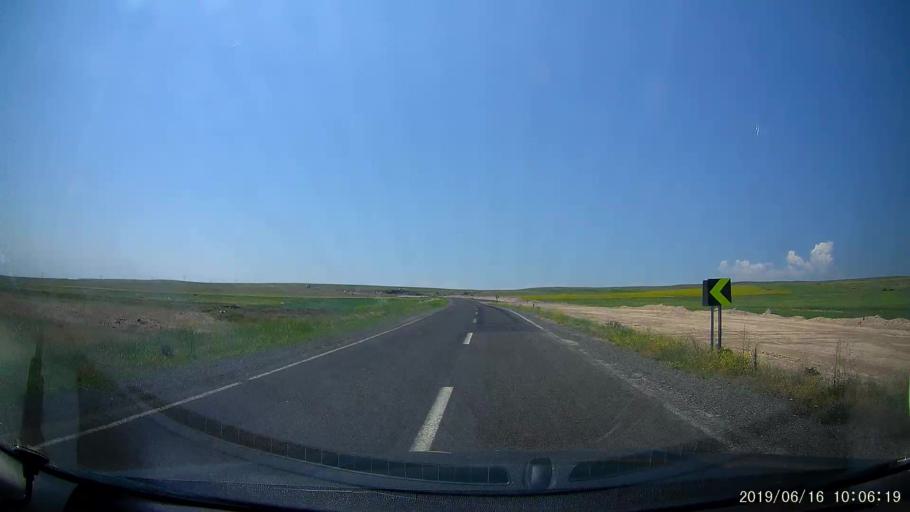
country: TR
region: Kars
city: Digor
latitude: 40.2569
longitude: 43.5417
